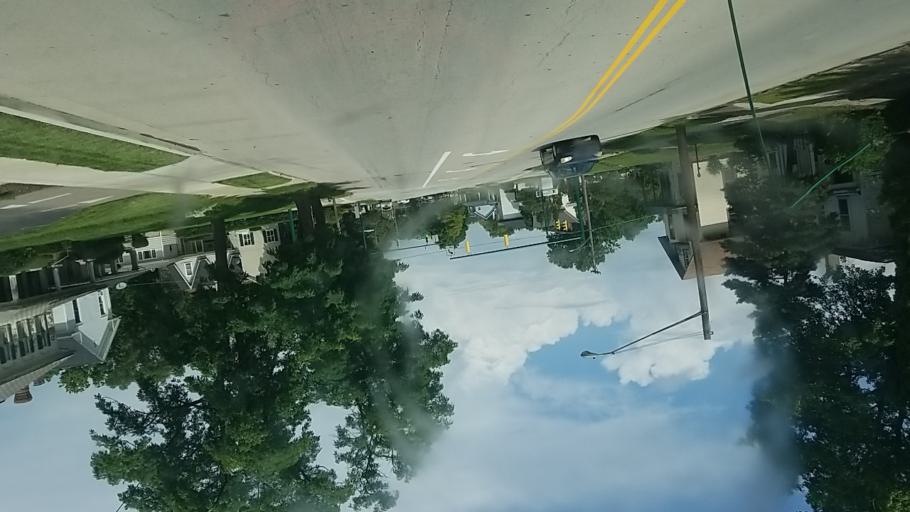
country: US
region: Ohio
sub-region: Champaign County
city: Urbana
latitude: 40.1118
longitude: -83.7520
